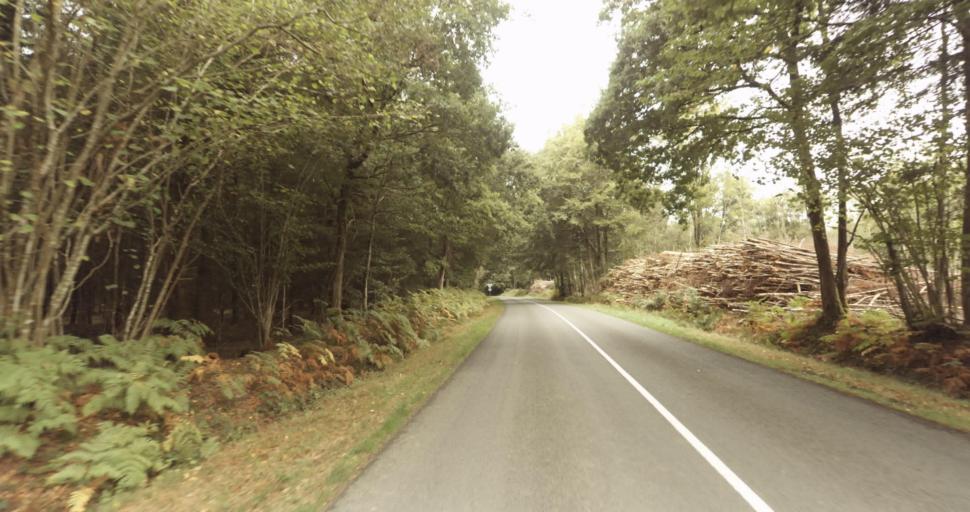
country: FR
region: Lower Normandy
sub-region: Departement de l'Orne
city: Gace
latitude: 48.7963
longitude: 0.3445
